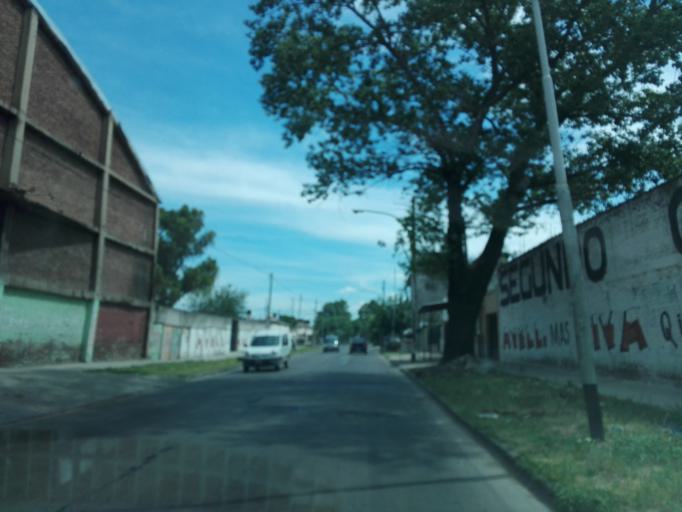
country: AR
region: Buenos Aires
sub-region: Partido de Lanus
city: Lanus
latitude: -34.6985
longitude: -58.3618
